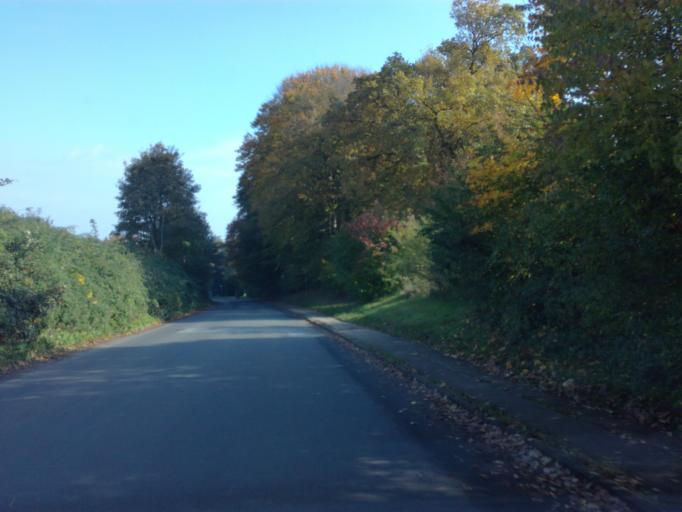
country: DK
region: South Denmark
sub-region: Vejle Kommune
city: Brejning
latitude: 55.6677
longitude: 9.6798
